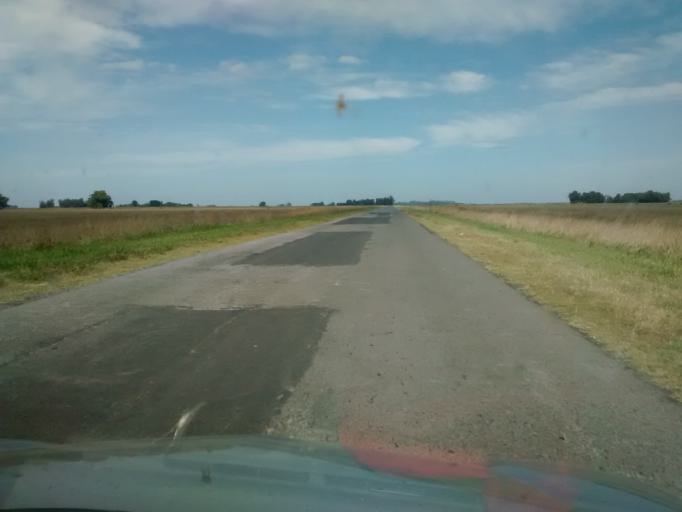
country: AR
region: Buenos Aires
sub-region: Partido de Ayacucho
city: Ayacucho
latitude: -37.1355
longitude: -58.5528
